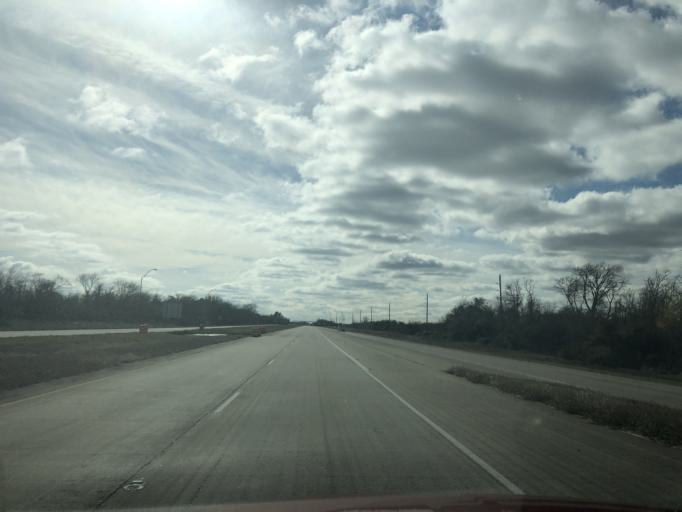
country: US
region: Texas
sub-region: Chambers County
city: Mont Belvieu
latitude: 29.7809
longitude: -94.8734
